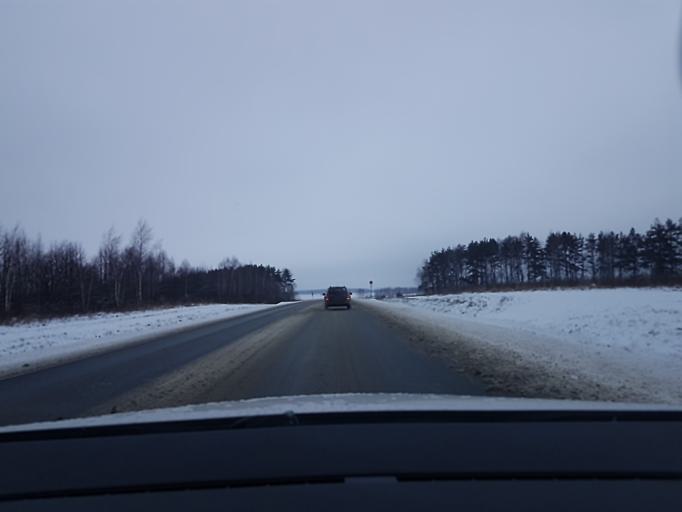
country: RU
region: Moskovskaya
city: Uzunovo
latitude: 54.5956
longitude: 38.4197
